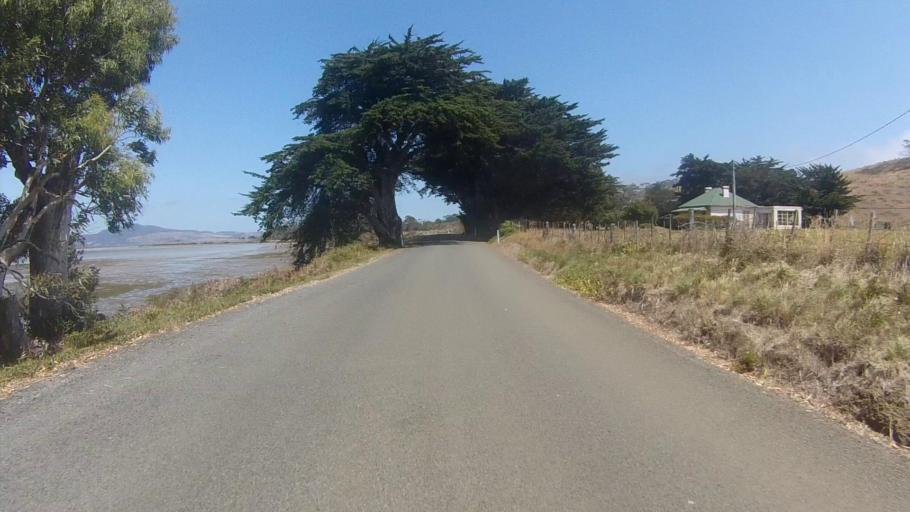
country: AU
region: Tasmania
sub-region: Sorell
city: Sorell
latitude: -42.8287
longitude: 147.8580
